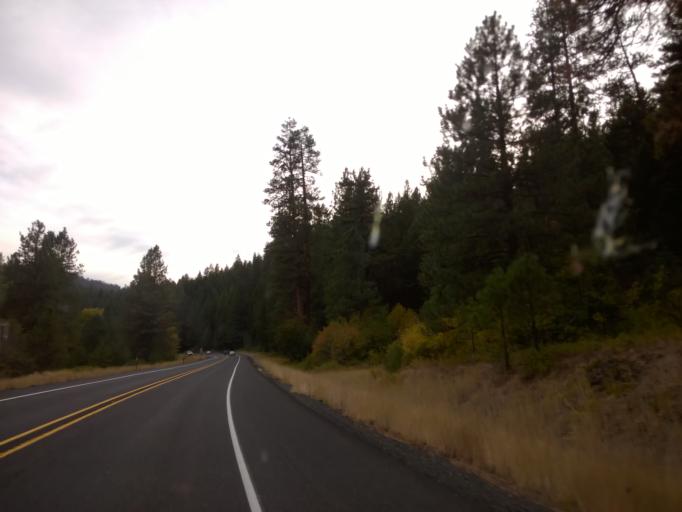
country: US
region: Washington
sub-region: Kittitas County
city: Cle Elum
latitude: 47.3026
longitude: -120.6976
